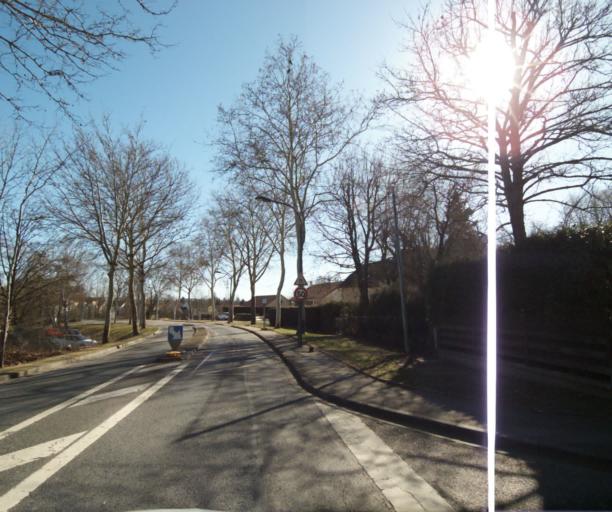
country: FR
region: Lorraine
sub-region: Departement de Meurthe-et-Moselle
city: Heillecourt
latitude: 48.6532
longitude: 6.2029
